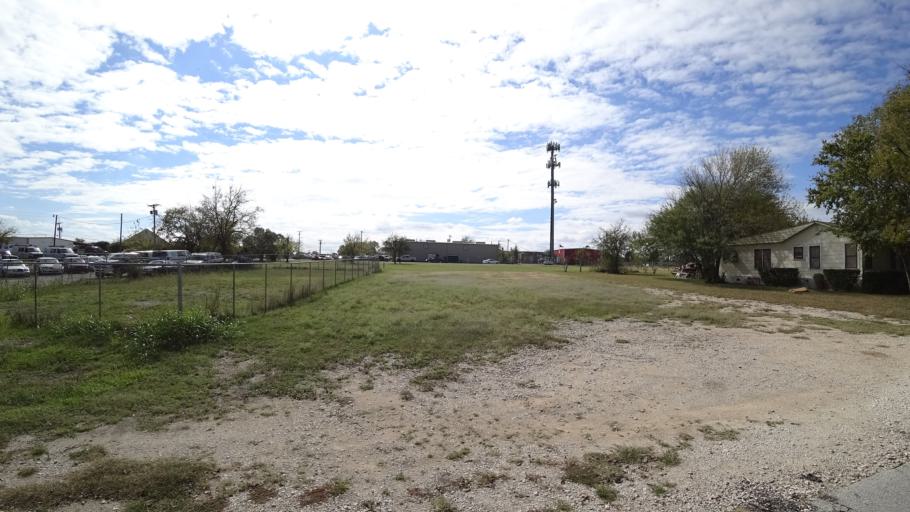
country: US
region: Texas
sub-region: Travis County
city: Pflugerville
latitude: 30.4464
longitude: -97.6302
